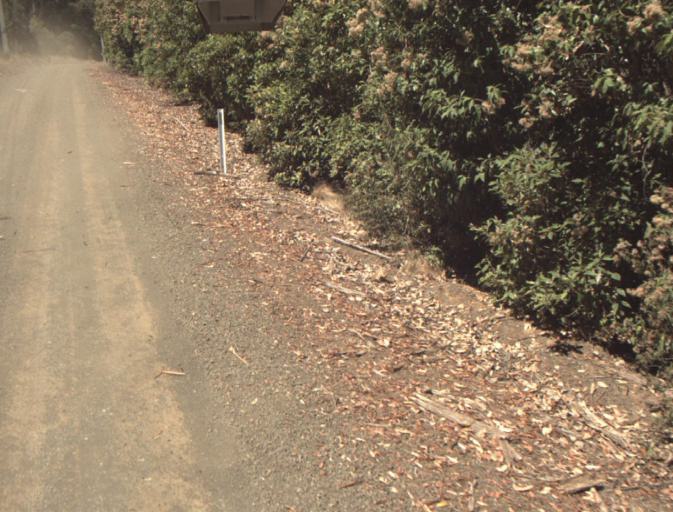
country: AU
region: Tasmania
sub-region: Dorset
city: Scottsdale
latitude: -41.3558
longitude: 147.3917
